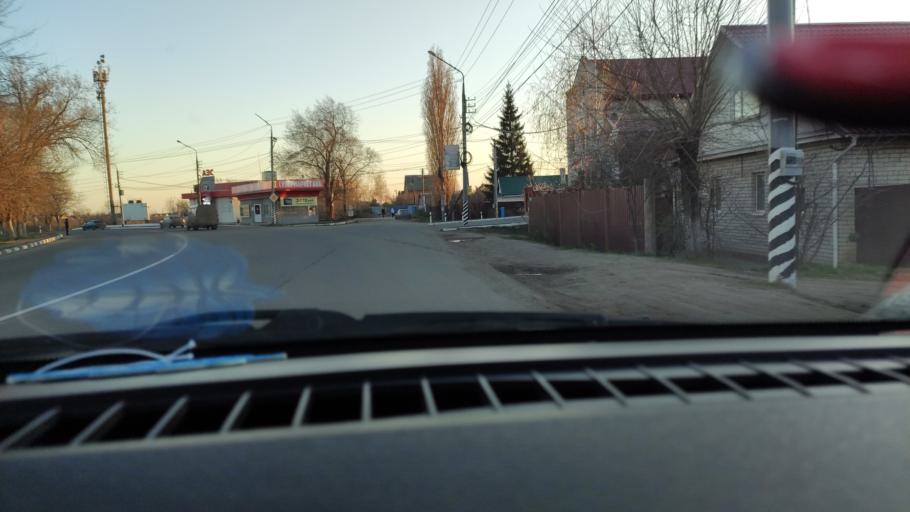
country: RU
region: Saratov
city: Privolzhskiy
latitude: 51.4226
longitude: 46.0469
